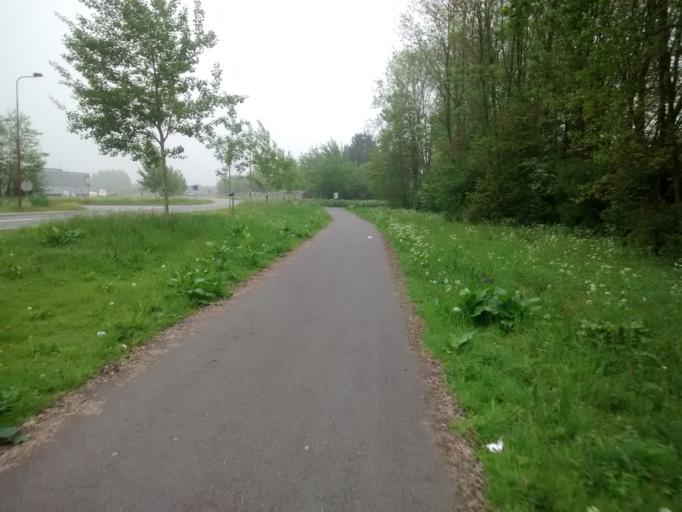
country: NL
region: Utrecht
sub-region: Gemeente Utrecht
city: Lunetten
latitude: 52.0500
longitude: 5.1204
